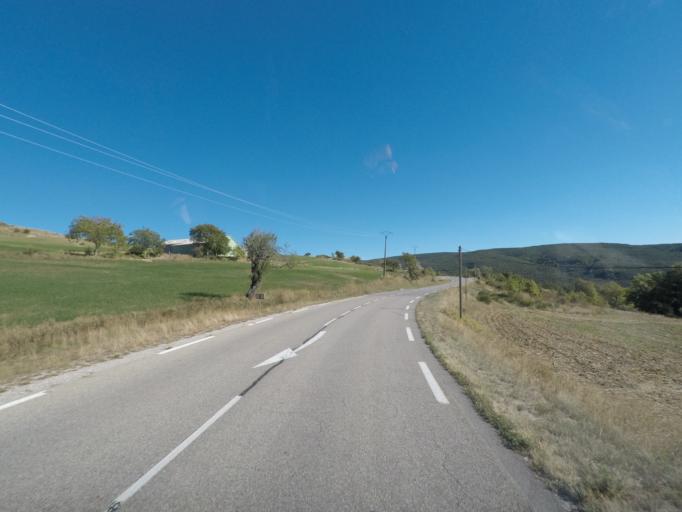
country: FR
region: Provence-Alpes-Cote d'Azur
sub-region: Departement des Hautes-Alpes
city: Serres
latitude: 44.4112
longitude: 5.5397
